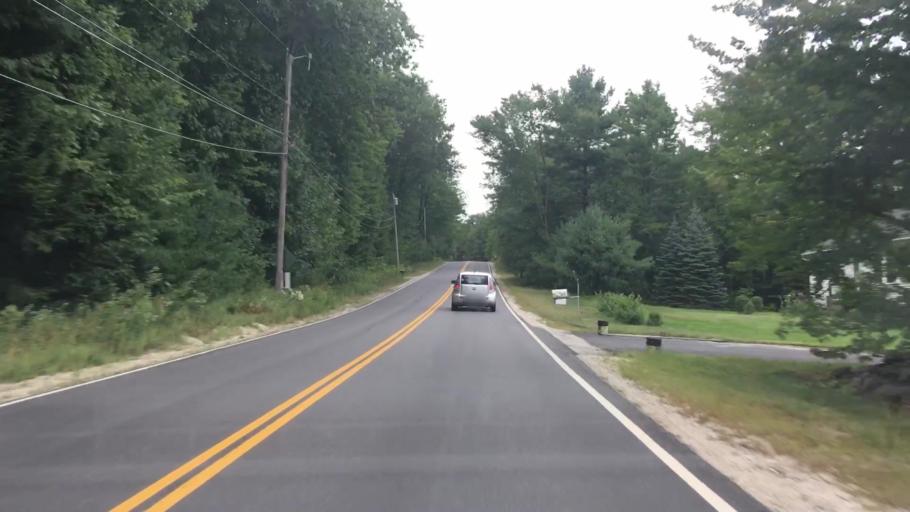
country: US
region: Maine
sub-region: Cumberland County
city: New Gloucester
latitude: 43.8886
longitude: -70.2530
